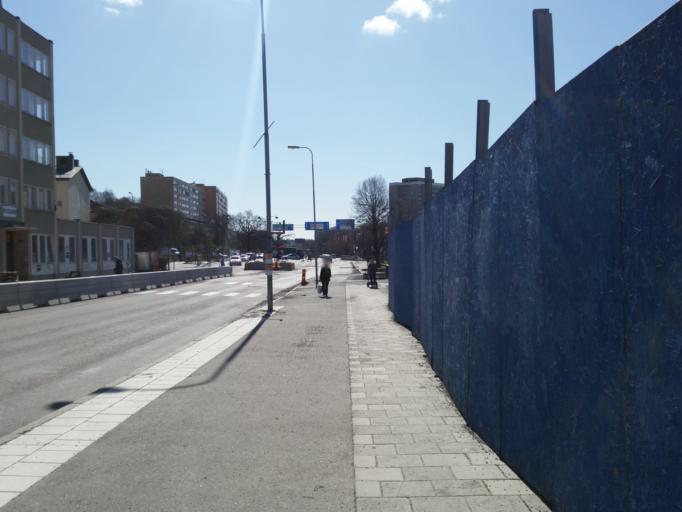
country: SE
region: Stockholm
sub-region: Solna Kommun
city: Solna
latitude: 59.3629
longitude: 17.9975
